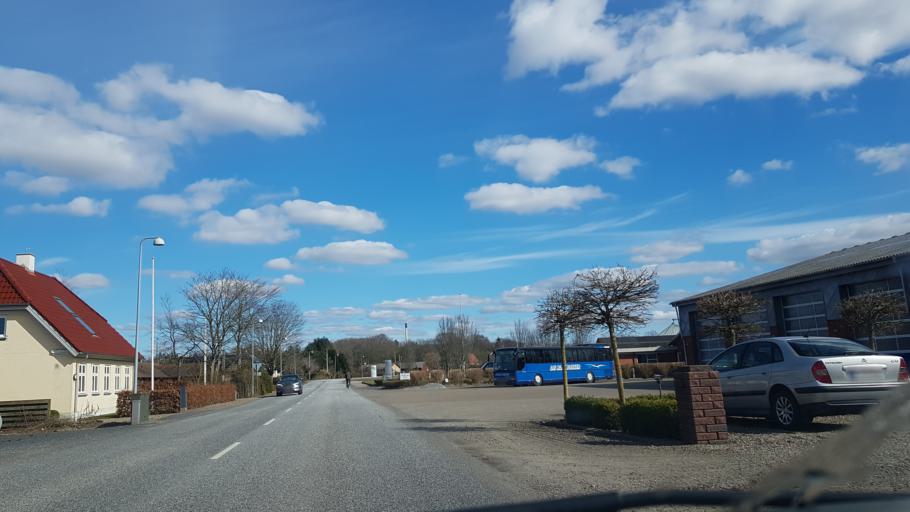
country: DK
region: South Denmark
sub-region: Esbjerg Kommune
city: Ribe
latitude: 55.3942
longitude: 8.7479
